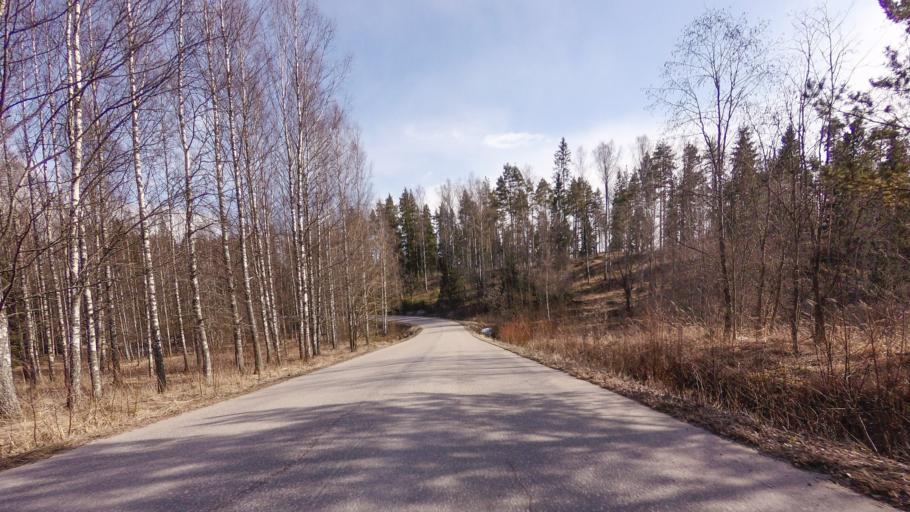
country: FI
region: Varsinais-Suomi
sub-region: Salo
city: Suomusjaervi
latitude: 60.2867
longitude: 23.6435
